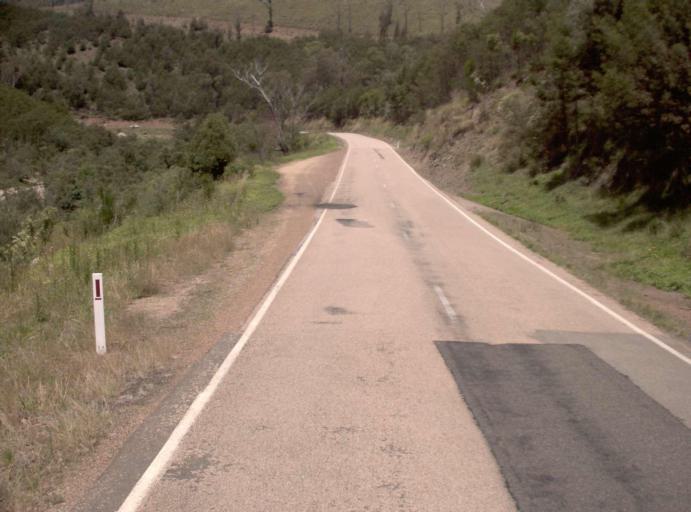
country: AU
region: Victoria
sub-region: East Gippsland
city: Bairnsdale
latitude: -37.5256
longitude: 147.8436
